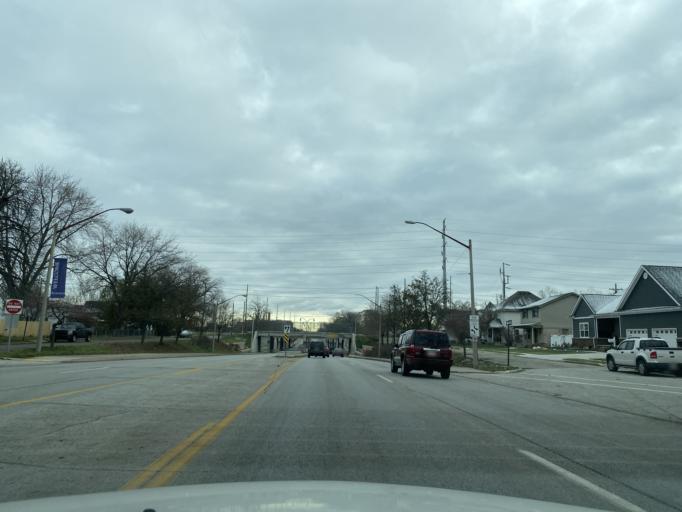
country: US
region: Michigan
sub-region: Wayne County
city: Wyandotte
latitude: 42.1997
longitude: -83.1652
